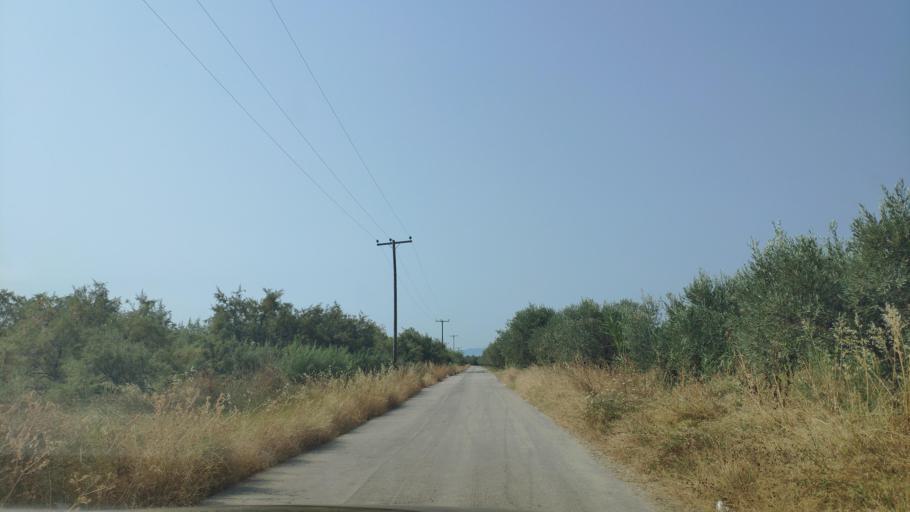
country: GR
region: West Greece
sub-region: Nomos Aitolias kai Akarnanias
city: Menidi
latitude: 39.0483
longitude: 21.0721
